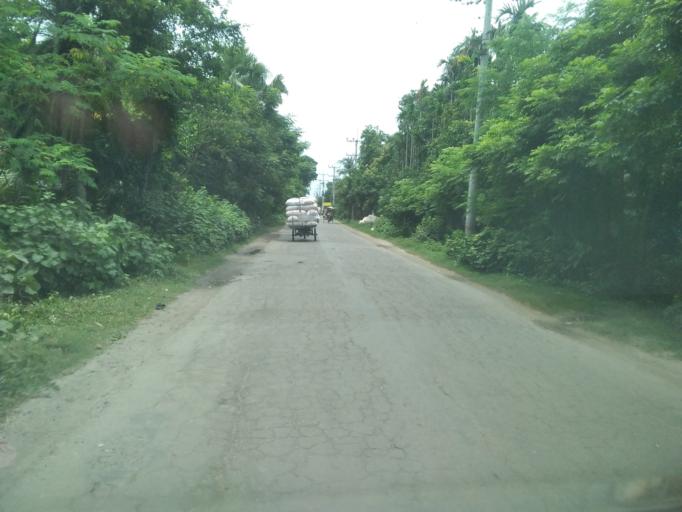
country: IN
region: West Bengal
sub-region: North 24 Parganas
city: Taki
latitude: 22.5733
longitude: 89.0001
